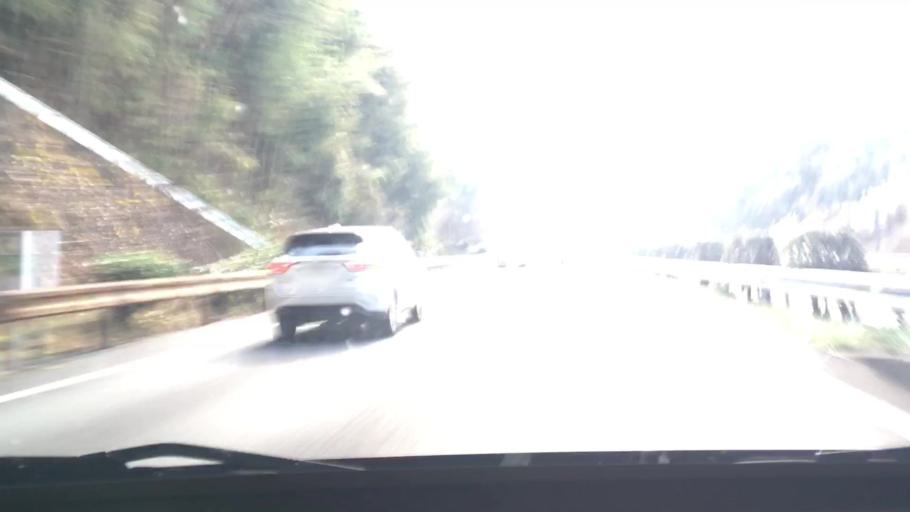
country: JP
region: Kumamoto
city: Uto
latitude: 32.6879
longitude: 130.7364
